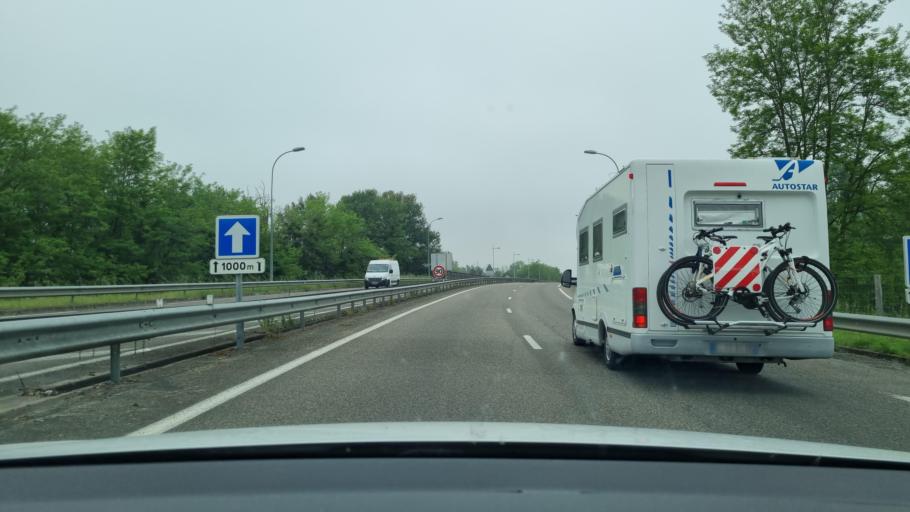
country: FR
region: Aquitaine
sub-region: Departement des Landes
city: Saint-Sever
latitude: 43.7655
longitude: -0.5589
